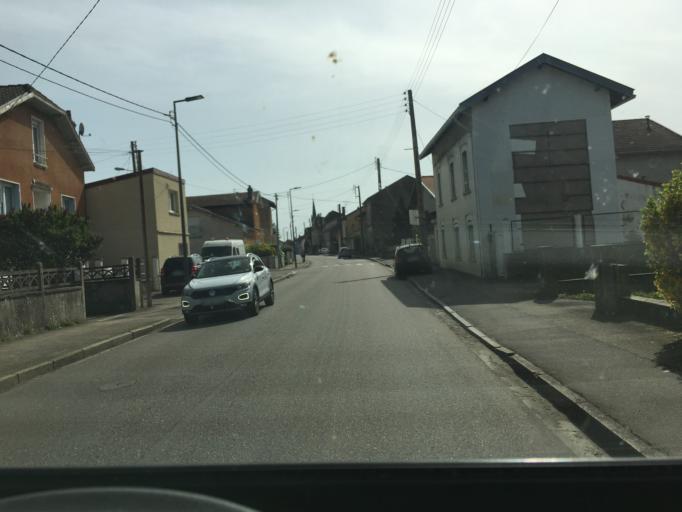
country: FR
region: Lorraine
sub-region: Departement de Meurthe-et-Moselle
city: Neuves-Maisons
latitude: 48.6166
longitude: 6.0956
